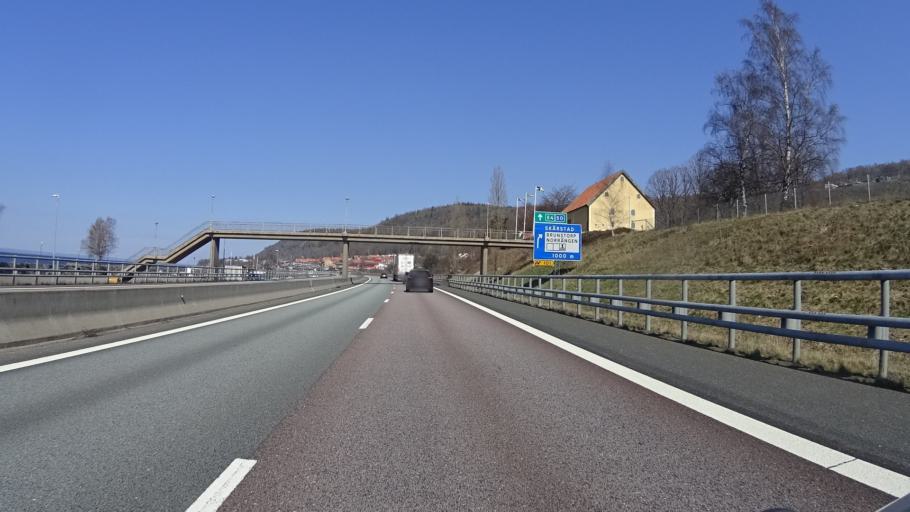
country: SE
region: Joenkoeping
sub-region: Jonkopings Kommun
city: Huskvarna
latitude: 57.7998
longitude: 14.2709
